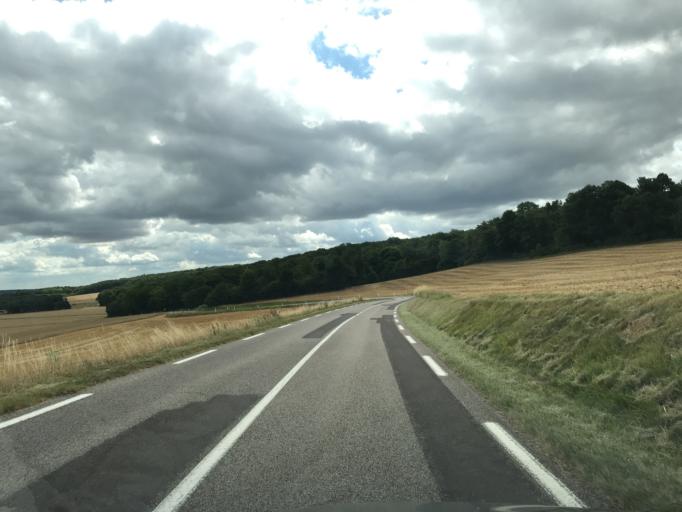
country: FR
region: Haute-Normandie
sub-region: Departement de l'Eure
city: Menilles
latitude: 49.0386
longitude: 1.2922
